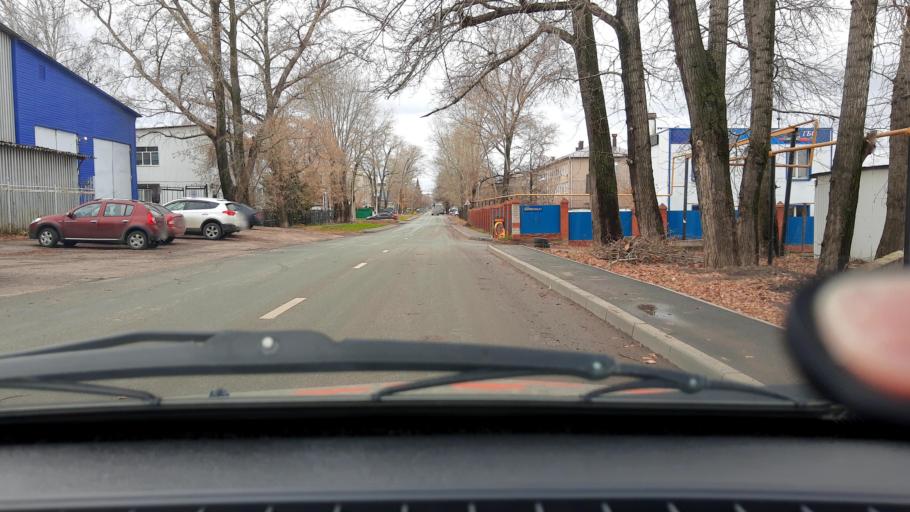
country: RU
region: Bashkortostan
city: Ufa
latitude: 54.8271
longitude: 56.0737
